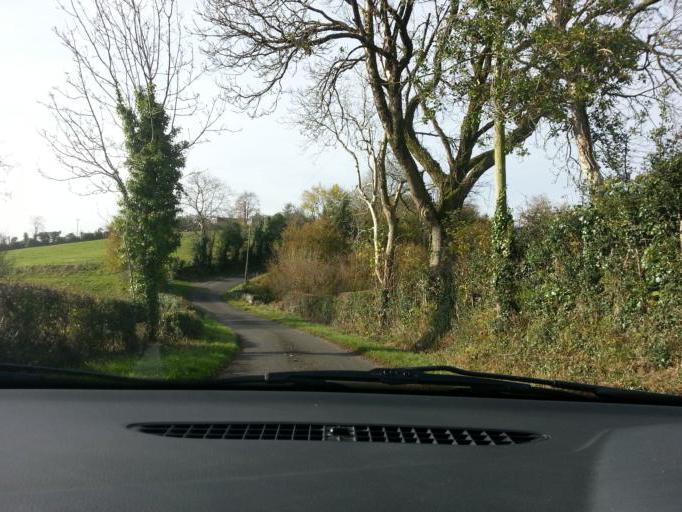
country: IE
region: Ulster
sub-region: County Monaghan
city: Clones
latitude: 54.2314
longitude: -7.2953
